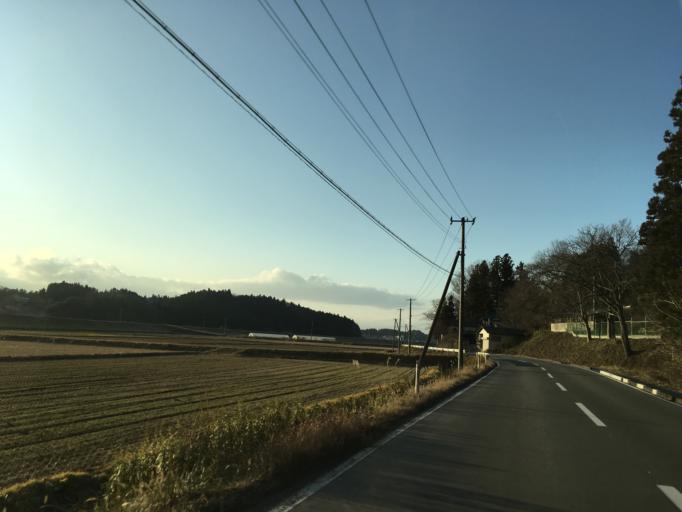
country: JP
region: Iwate
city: Ichinoseki
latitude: 38.8078
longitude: 141.2184
